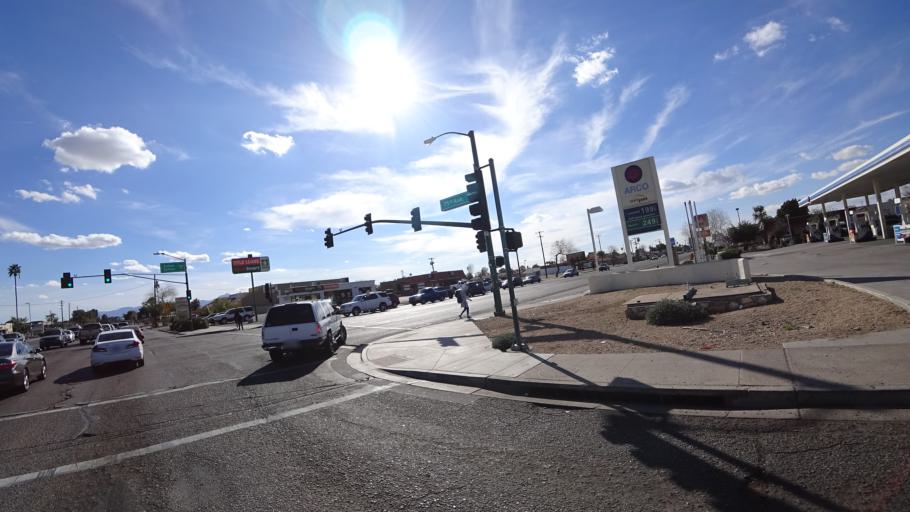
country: US
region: Arizona
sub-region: Maricopa County
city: Glendale
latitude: 33.4949
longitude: -112.2207
